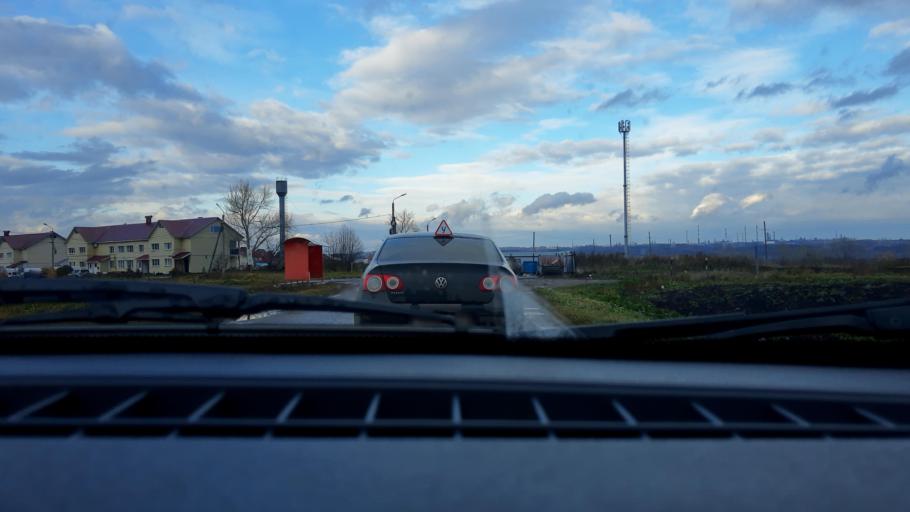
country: RU
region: Bashkortostan
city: Ufa
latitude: 54.8509
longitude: 56.0129
